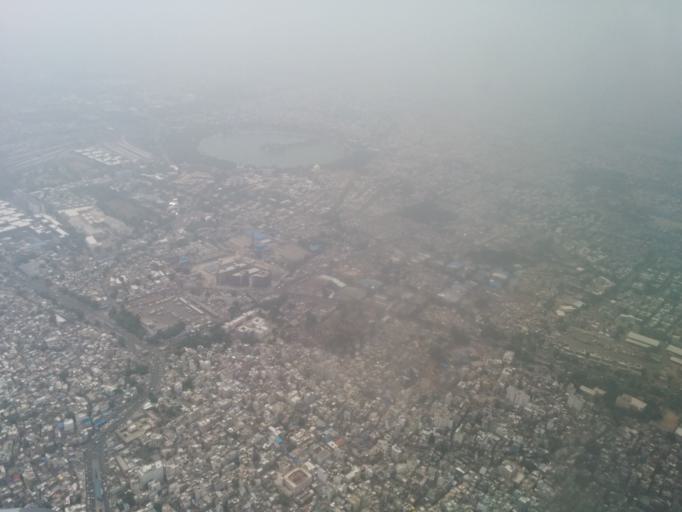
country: IN
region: Gujarat
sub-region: Ahmadabad
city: Ahmedabad
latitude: 23.0217
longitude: 72.5823
